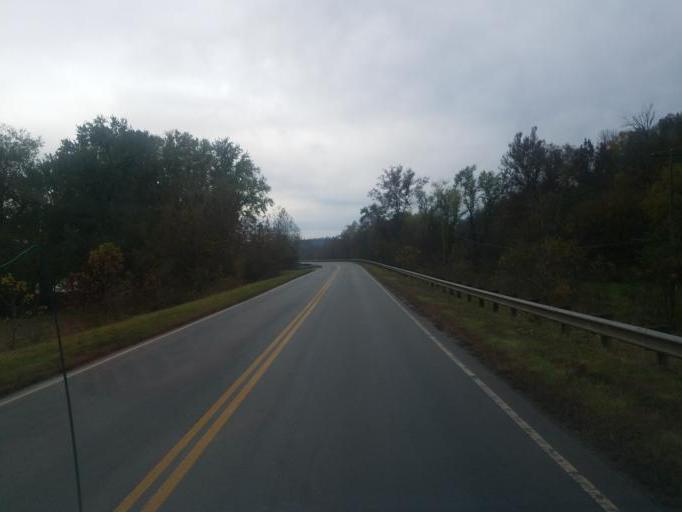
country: US
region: Ohio
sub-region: Washington County
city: Beverly
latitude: 39.5505
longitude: -81.6486
